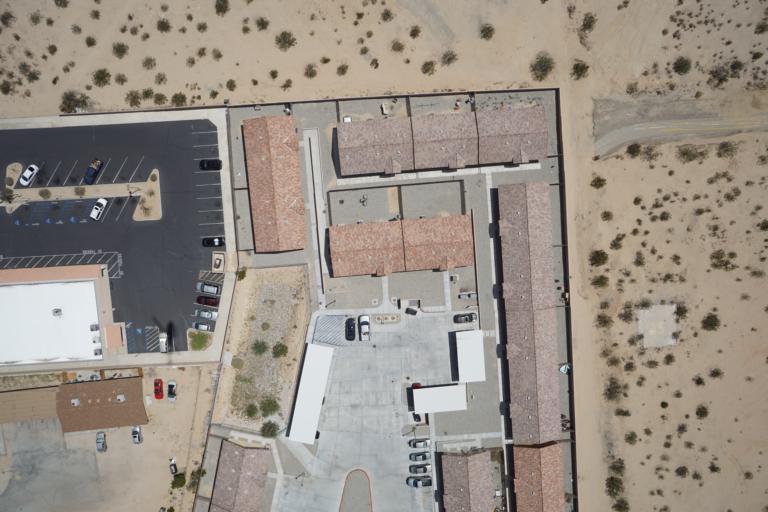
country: US
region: California
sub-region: San Bernardino County
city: Twentynine Palms
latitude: 34.1432
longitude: -116.0556
